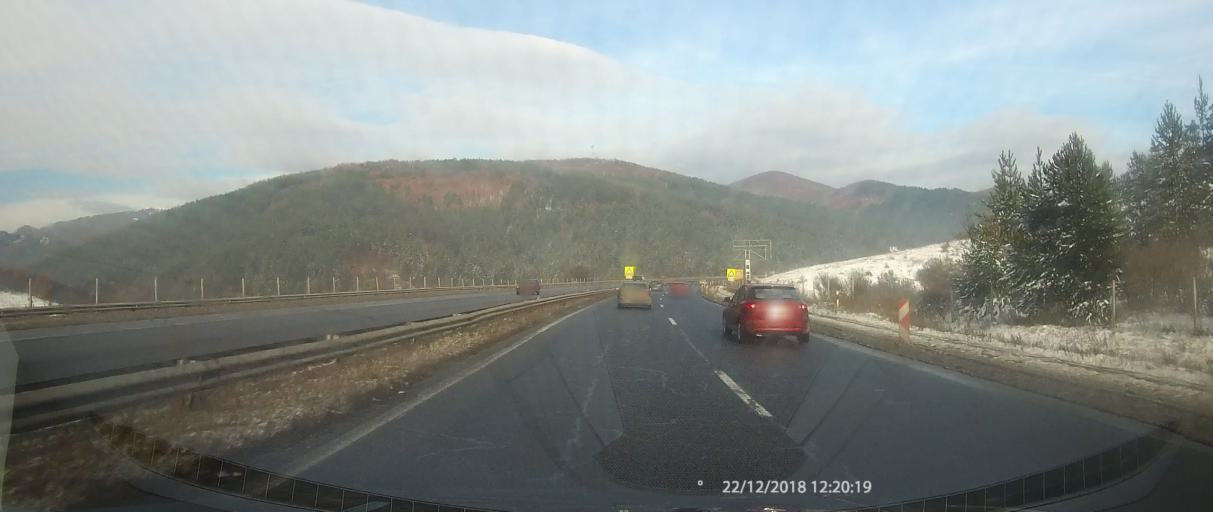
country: BG
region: Sofiya
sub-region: Obshtina Gorna Malina
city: Gorna Malina
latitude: 42.7437
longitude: 23.6602
